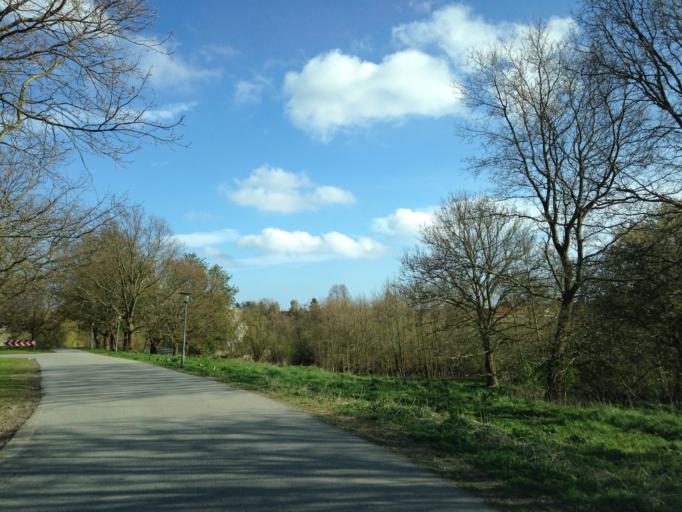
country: DK
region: Zealand
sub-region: Greve Kommune
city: Greve
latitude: 55.5784
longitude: 12.2715
